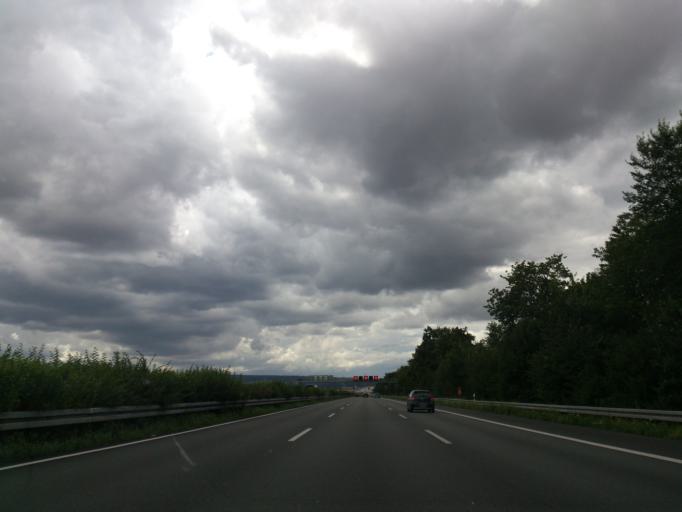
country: DE
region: Lower Saxony
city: Rodenberg
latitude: 52.2986
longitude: 9.3672
